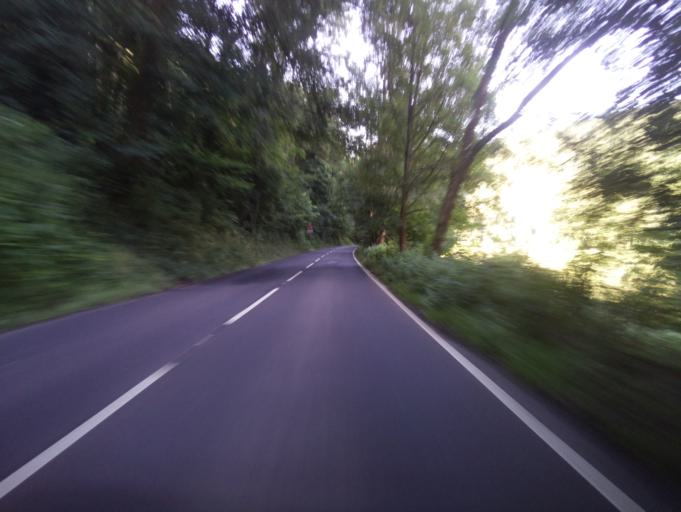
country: GB
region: Wales
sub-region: Monmouthshire
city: Monmouth
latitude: 51.7735
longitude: -2.6765
